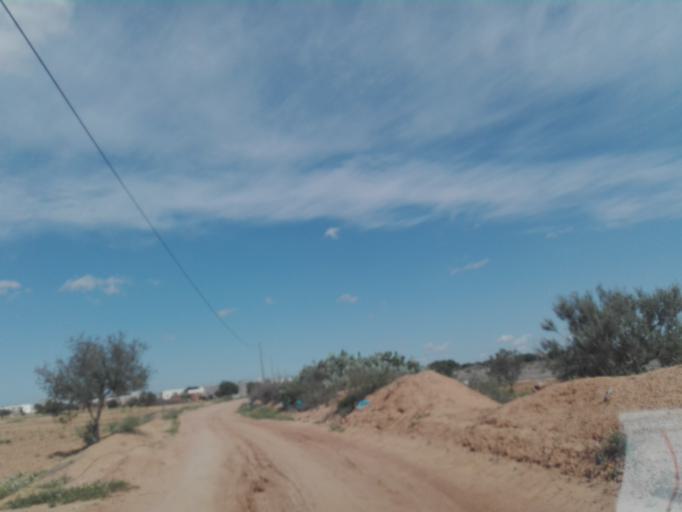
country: TN
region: Safaqis
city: Sfax
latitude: 34.7306
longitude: 10.5093
